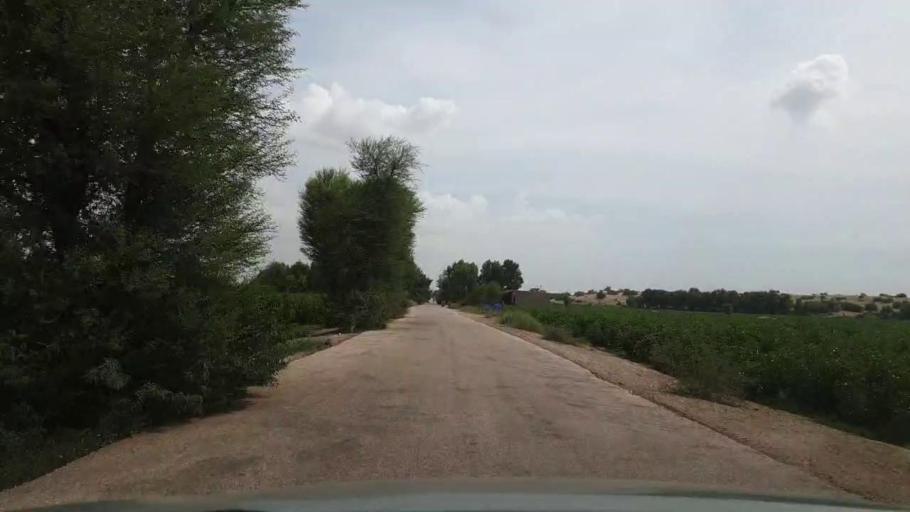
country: PK
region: Sindh
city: Kot Diji
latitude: 27.1628
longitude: 69.0350
